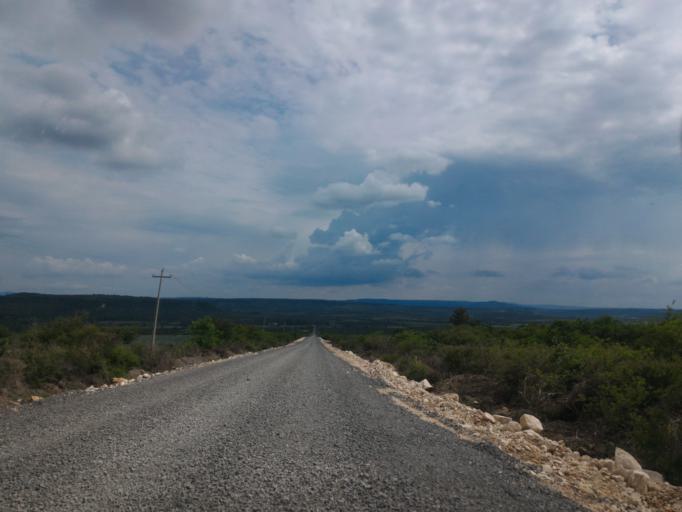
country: MX
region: Jalisco
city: San Diego de Alejandria
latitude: 20.9130
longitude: -102.0446
